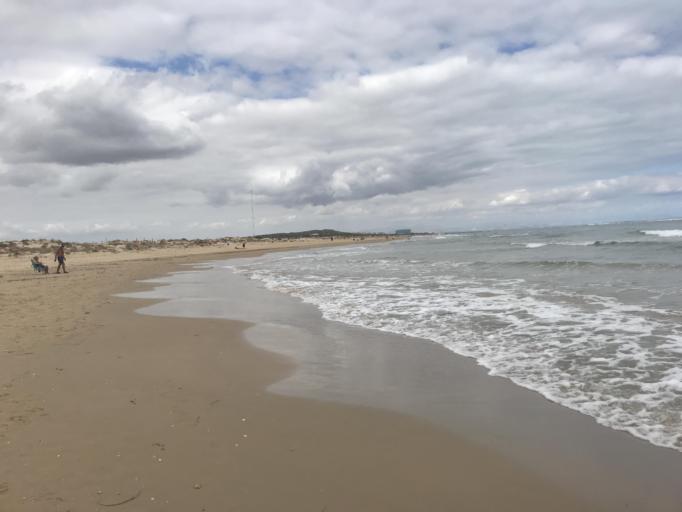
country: ES
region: Valencia
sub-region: Provincia de Alicante
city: Guardamar del Segura
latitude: 38.0334
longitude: -0.6516
